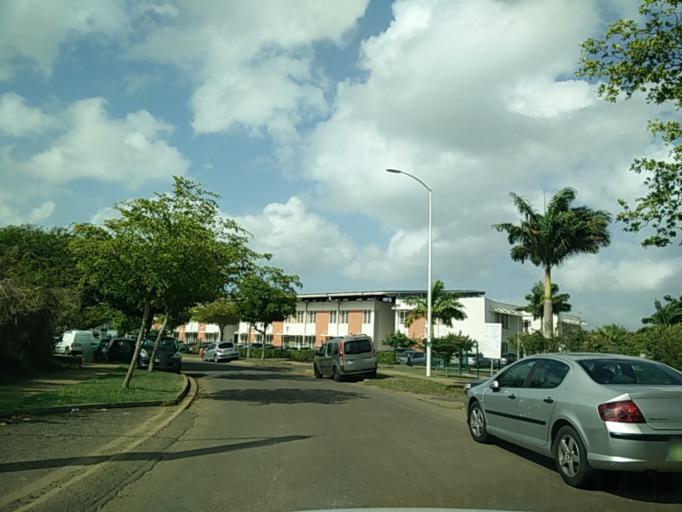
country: GP
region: Guadeloupe
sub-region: Guadeloupe
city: Les Abymes
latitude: 16.2764
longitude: -61.5121
